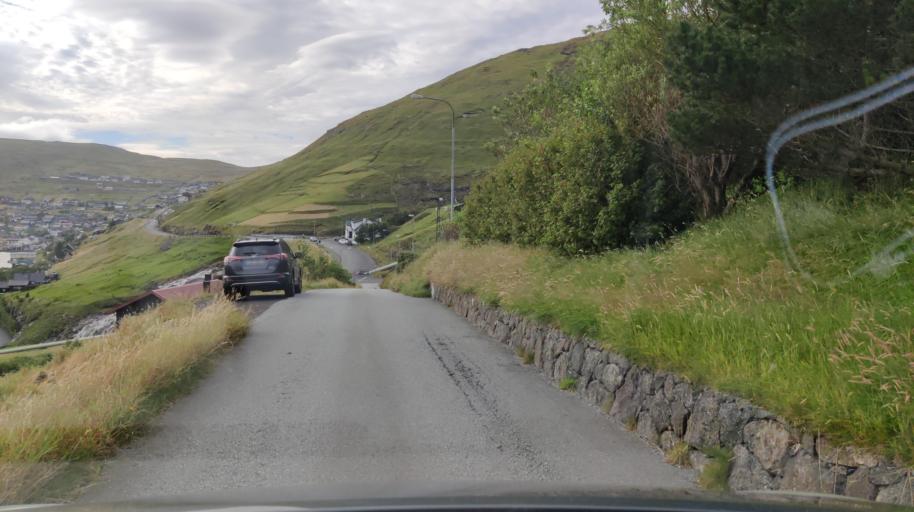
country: FO
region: Streymoy
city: Vestmanna
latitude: 62.1550
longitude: -7.1454
